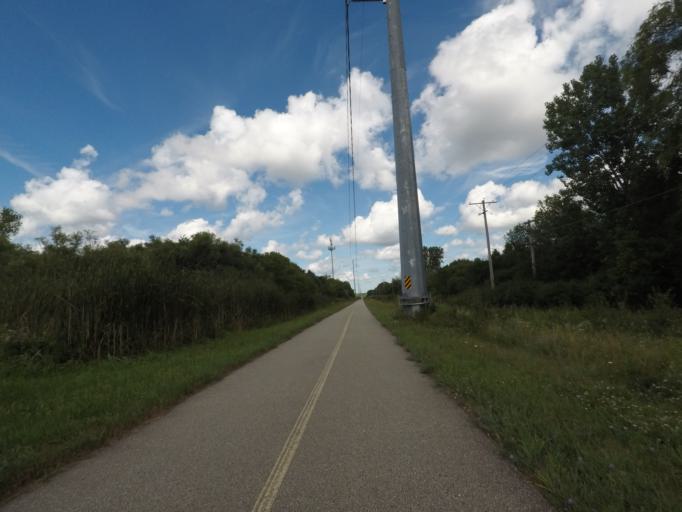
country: US
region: Wisconsin
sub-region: Waukesha County
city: Pewaukee
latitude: 43.0498
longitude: -88.2756
